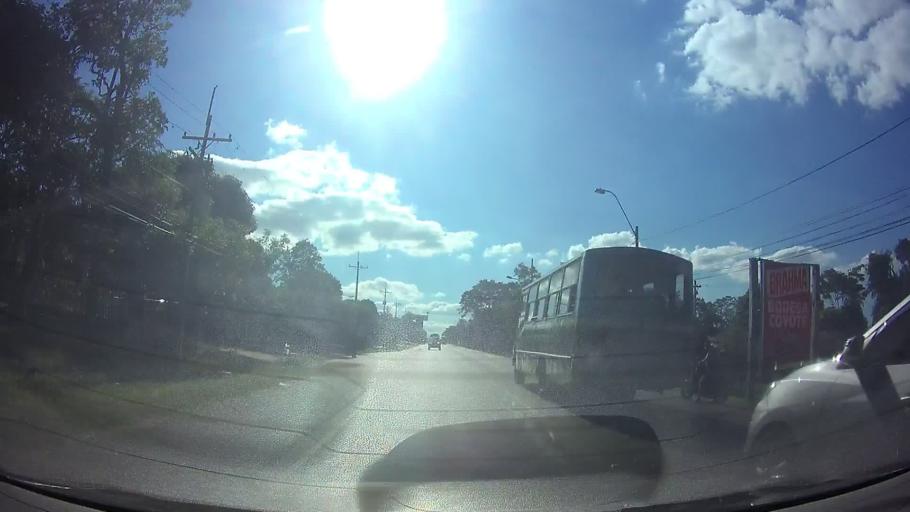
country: PY
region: Cordillera
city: Caacupe
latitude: -25.3896
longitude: -57.1663
